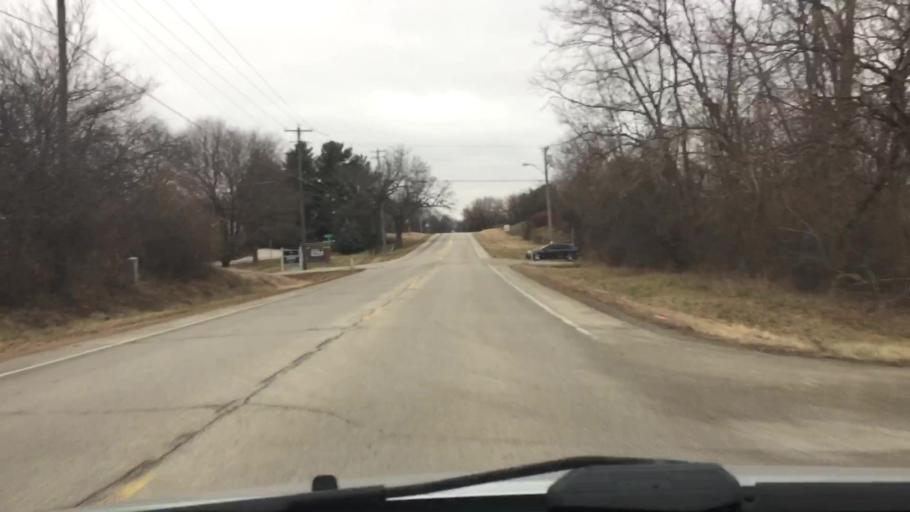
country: US
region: Wisconsin
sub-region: Waukesha County
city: Nashotah
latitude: 43.0833
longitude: -88.4033
